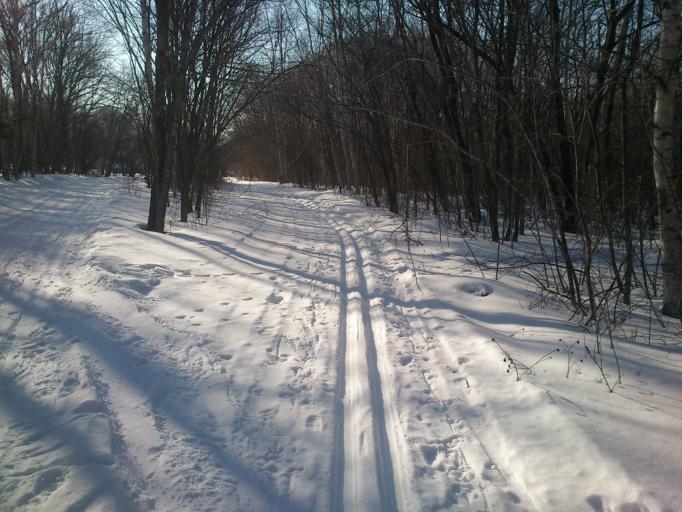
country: RU
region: Primorskiy
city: Volchanets
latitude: 43.1687
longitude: 132.7272
